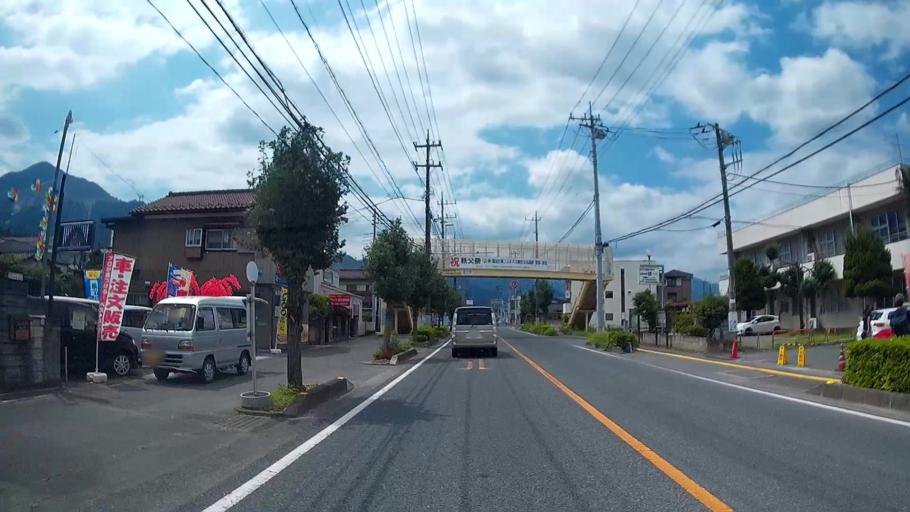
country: JP
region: Saitama
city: Chichibu
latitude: 35.9871
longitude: 139.0837
